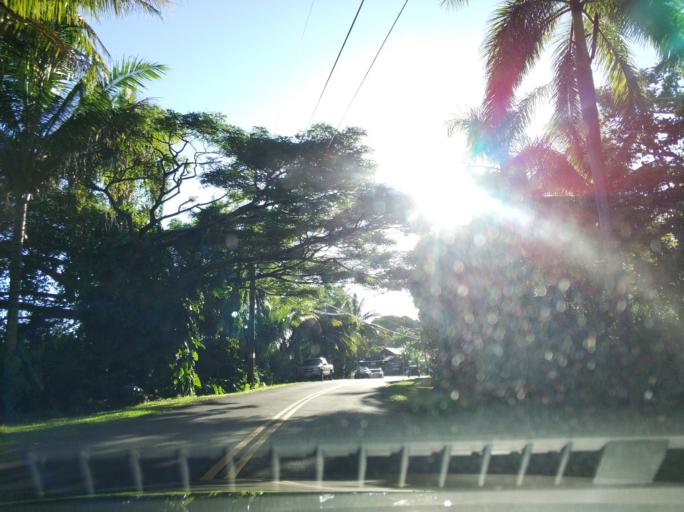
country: US
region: Hawaii
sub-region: Hawaii County
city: Leilani Estates
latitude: 19.3617
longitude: -154.9695
